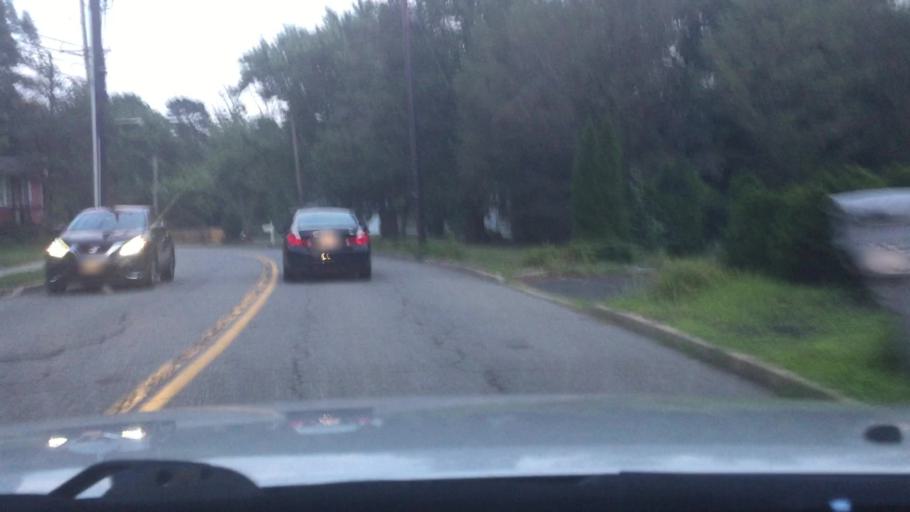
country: US
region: New Jersey
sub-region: Middlesex County
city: Milltown
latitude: 40.4289
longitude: -74.4497
